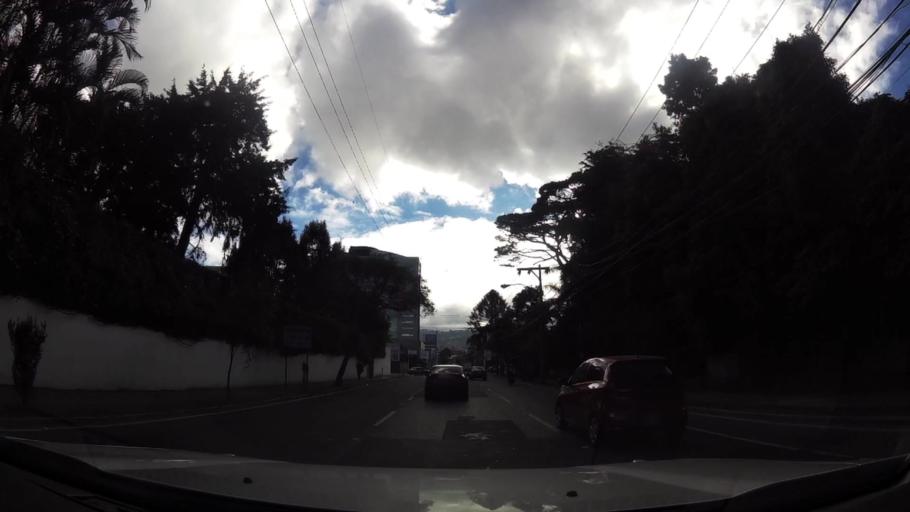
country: GT
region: Guatemala
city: Santa Catarina Pinula
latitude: 14.5885
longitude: -90.5063
